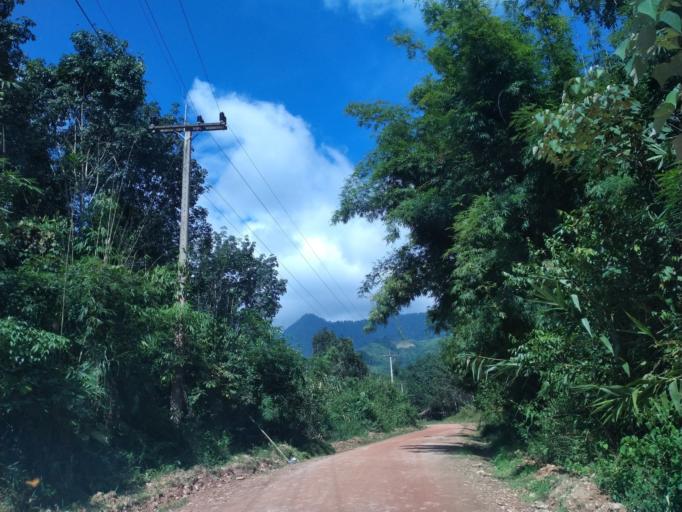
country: TH
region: Nong Khai
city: Rattanawapi
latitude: 18.6360
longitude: 102.9582
